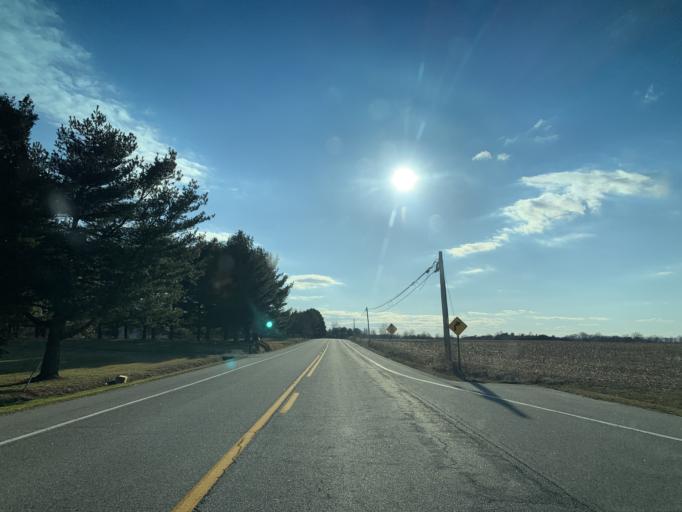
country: US
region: Maryland
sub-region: Queen Anne's County
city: Kingstown
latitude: 39.1508
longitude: -75.9663
